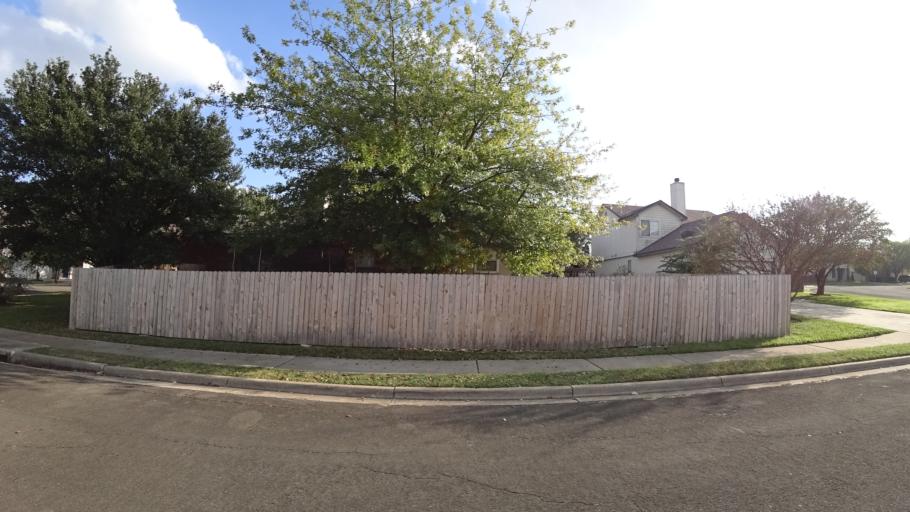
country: US
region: Texas
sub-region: Williamson County
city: Round Rock
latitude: 30.4913
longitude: -97.6614
